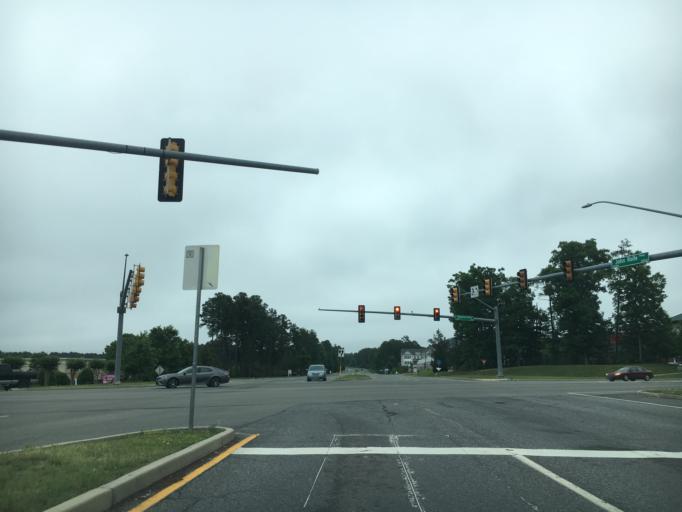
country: US
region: Virginia
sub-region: Henrico County
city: Short Pump
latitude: 37.6202
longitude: -77.6235
